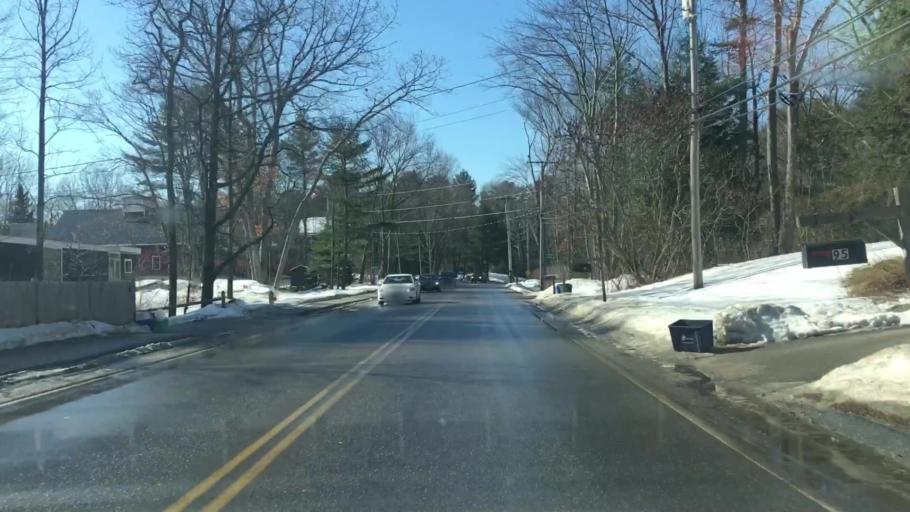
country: US
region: Maine
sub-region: Cumberland County
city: Falmouth
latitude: 43.7240
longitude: -70.2564
